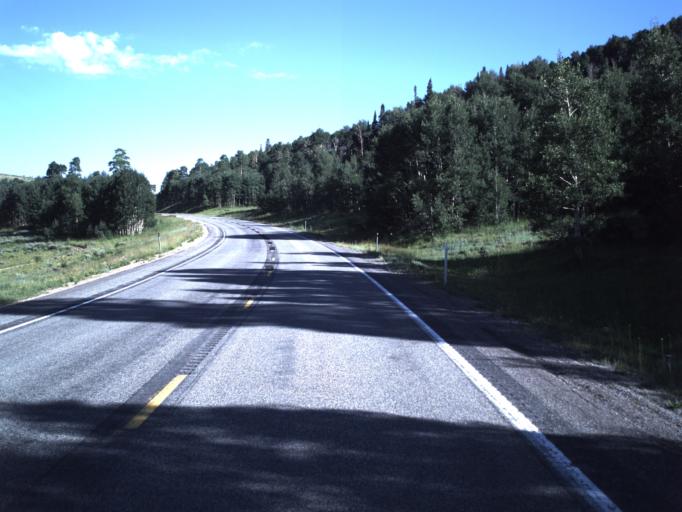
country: US
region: Utah
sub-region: Sanpete County
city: Fairview
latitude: 39.6035
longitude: -111.2744
